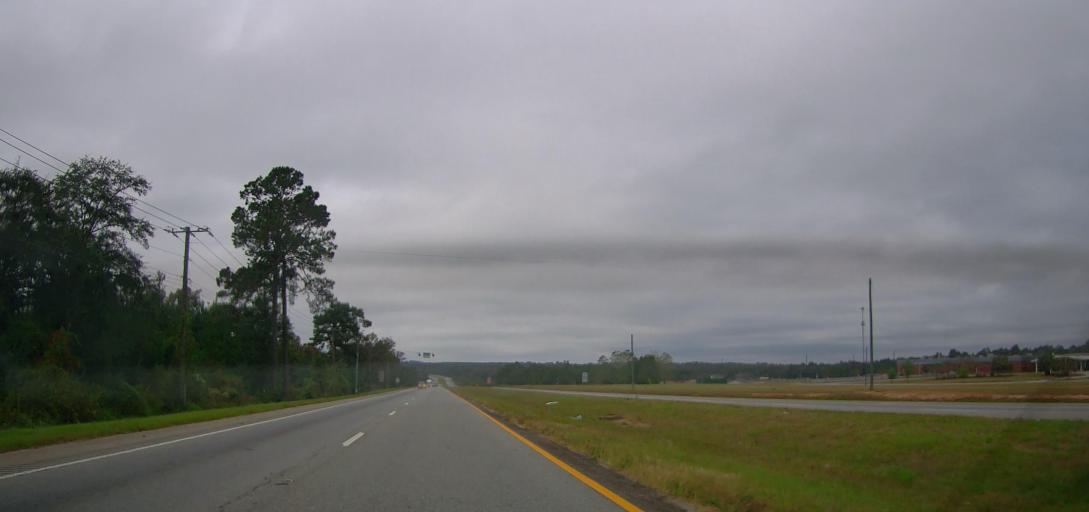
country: US
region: Georgia
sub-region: Thomas County
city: Thomasville
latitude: 30.8748
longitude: -83.9690
